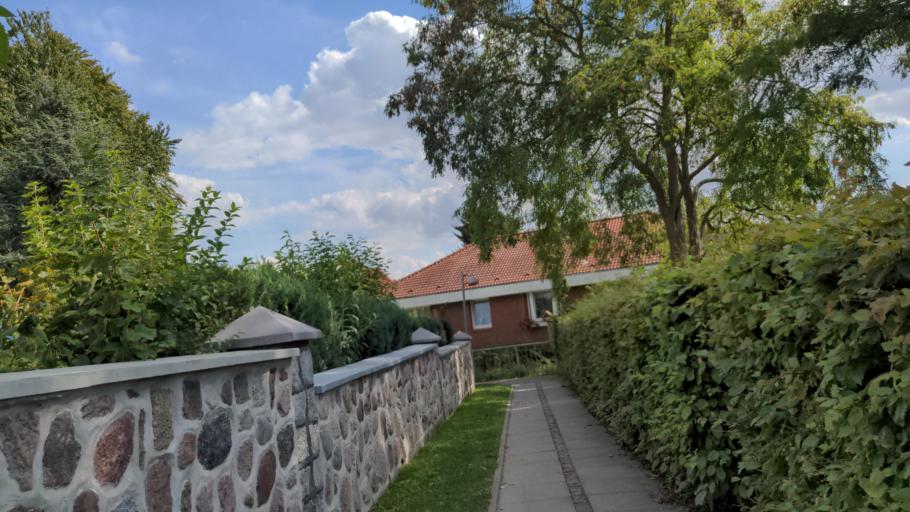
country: DE
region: Mecklenburg-Vorpommern
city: Klutz
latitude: 53.9666
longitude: 11.1620
